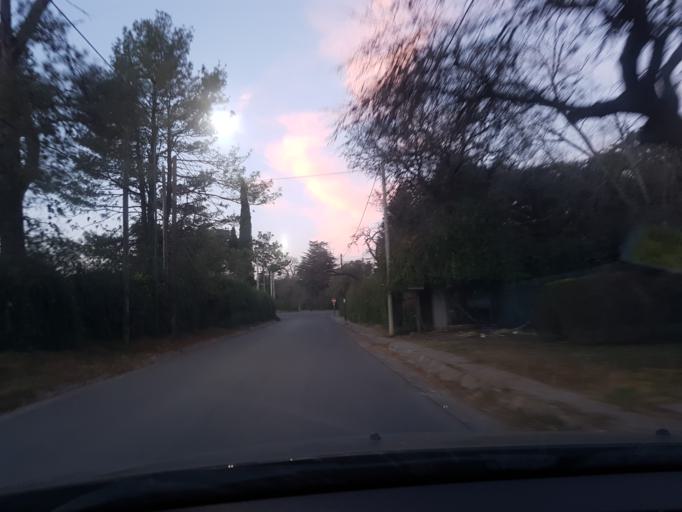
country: AR
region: Cordoba
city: Villa Allende
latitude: -31.2812
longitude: -64.2860
